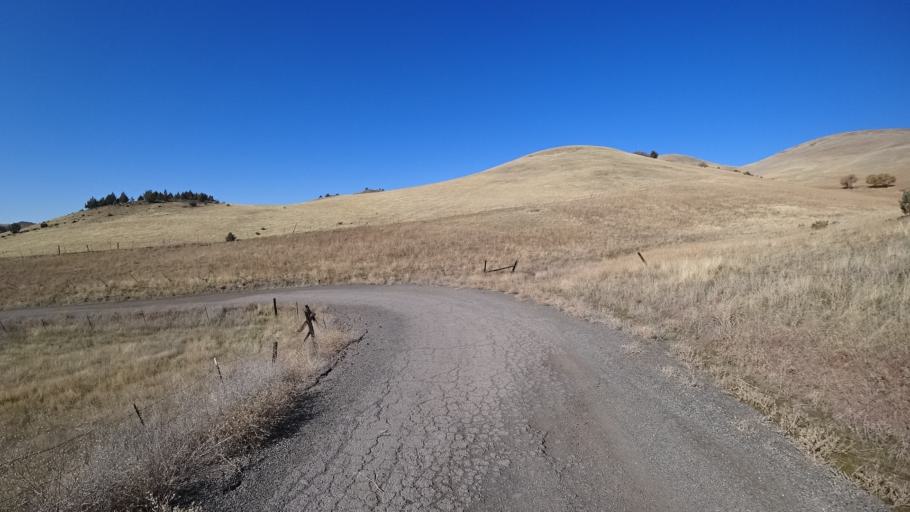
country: US
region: California
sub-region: Siskiyou County
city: Montague
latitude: 41.7943
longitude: -122.3417
